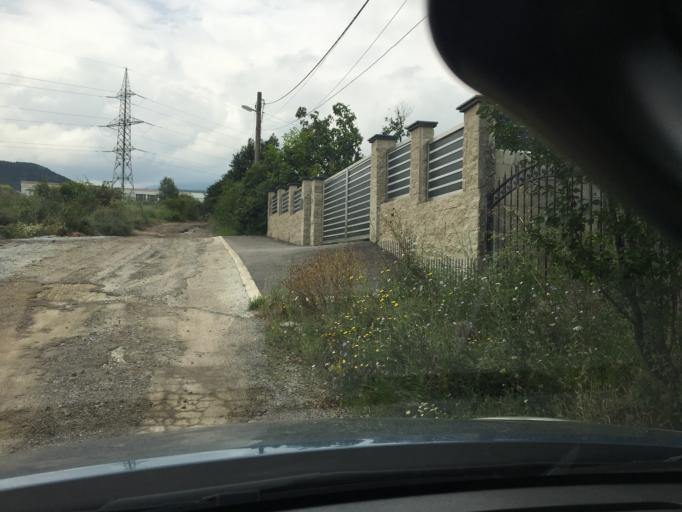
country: BG
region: Sofia-Capital
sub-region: Stolichna Obshtina
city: Sofia
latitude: 42.6163
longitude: 23.3614
